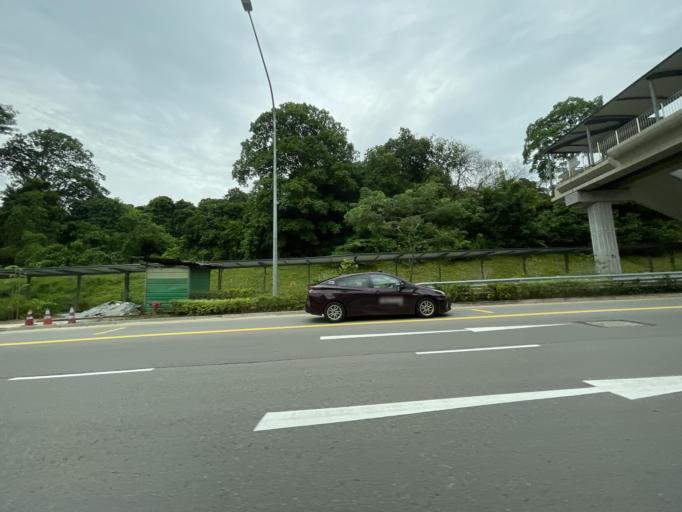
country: SG
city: Singapore
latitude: 1.3438
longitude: 103.7763
